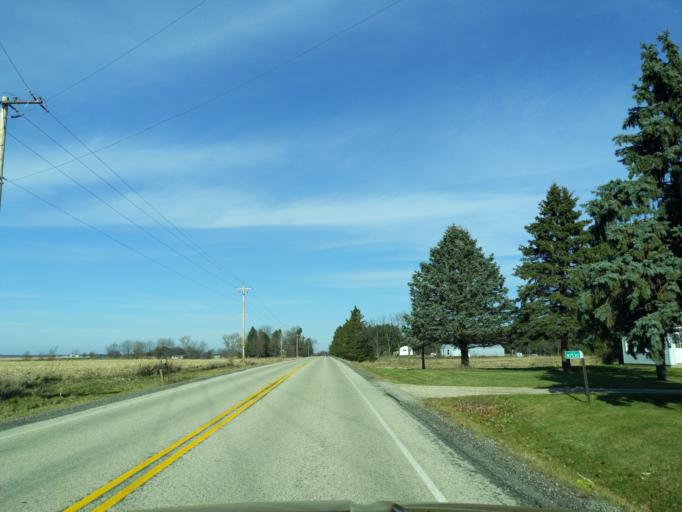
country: US
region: Wisconsin
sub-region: Walworth County
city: Elkhorn
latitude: 42.7641
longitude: -88.6030
